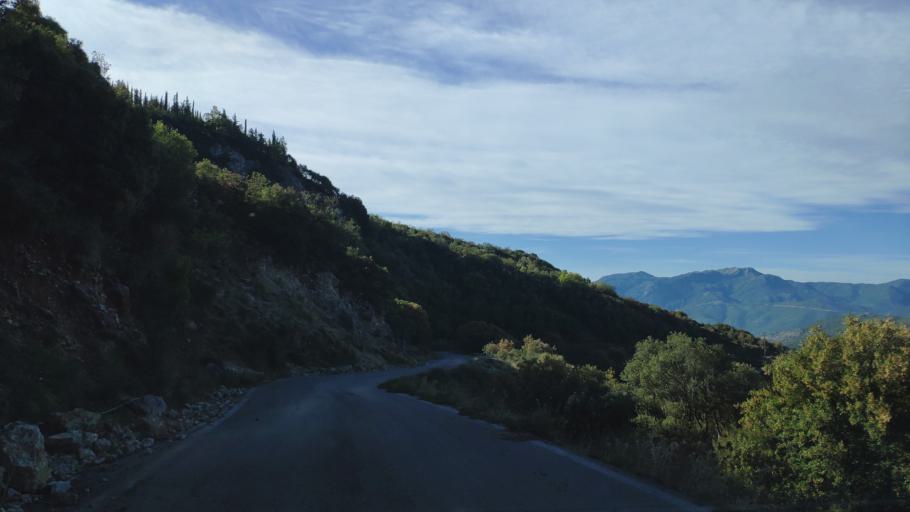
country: GR
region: Peloponnese
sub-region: Nomos Arkadias
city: Dimitsana
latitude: 37.5506
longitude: 22.0604
